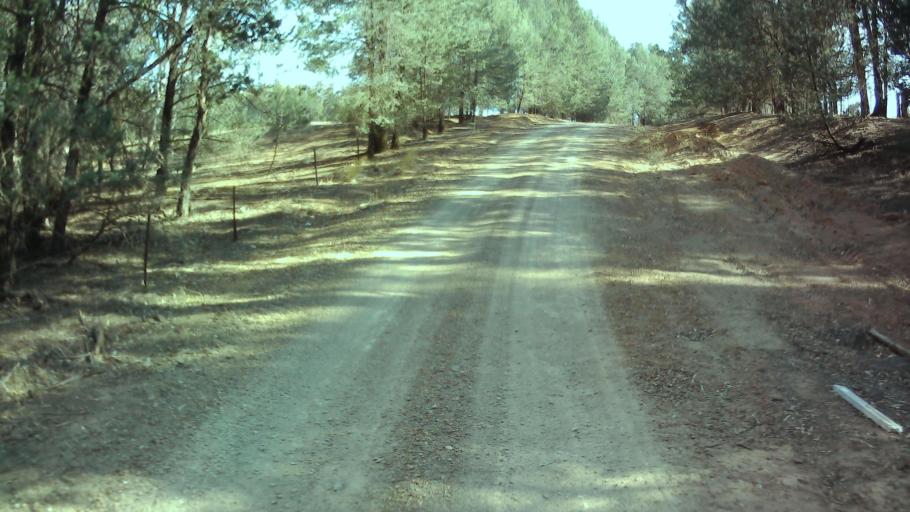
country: AU
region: New South Wales
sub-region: Weddin
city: Grenfell
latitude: -33.7704
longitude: 148.0469
